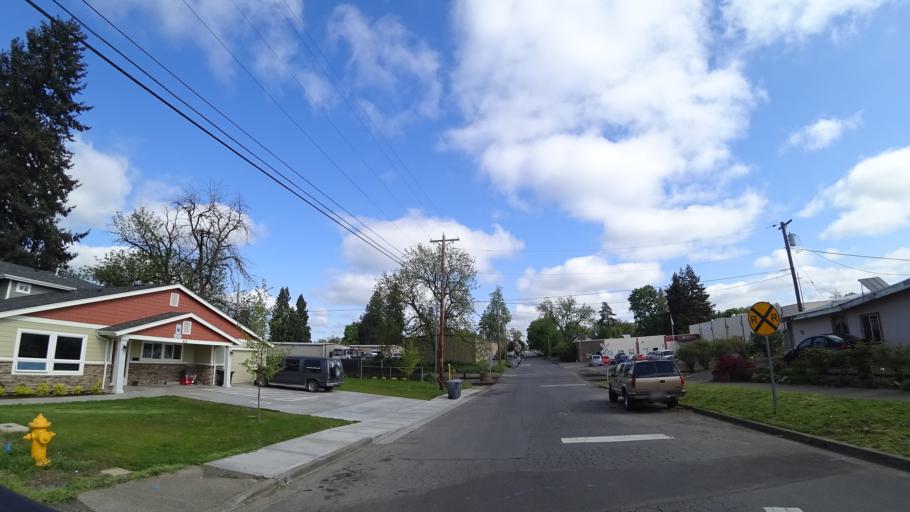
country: US
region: Oregon
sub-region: Washington County
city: Hillsboro
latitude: 45.5158
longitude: -122.9864
